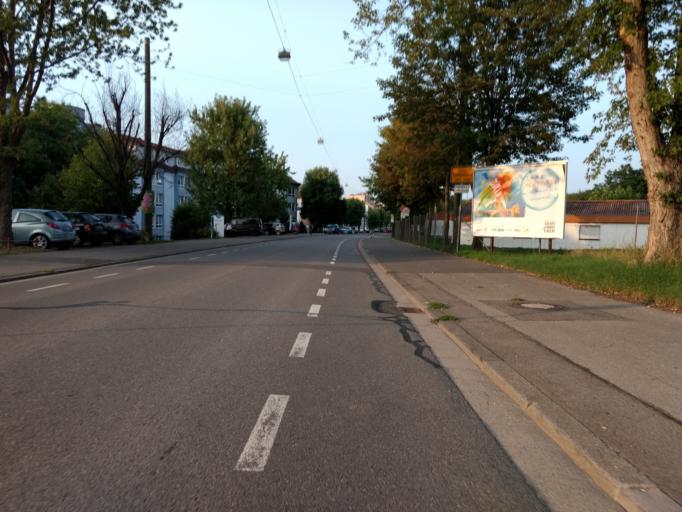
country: DE
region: Saarland
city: Wallerfangen
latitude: 49.3410
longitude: 6.7167
